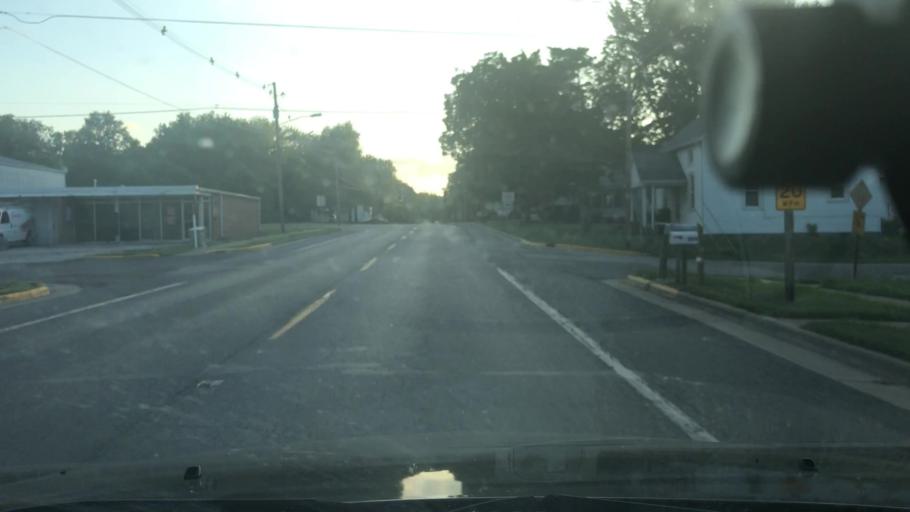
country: US
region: Illinois
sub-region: Washington County
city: Okawville
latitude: 38.4360
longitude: -89.5494
